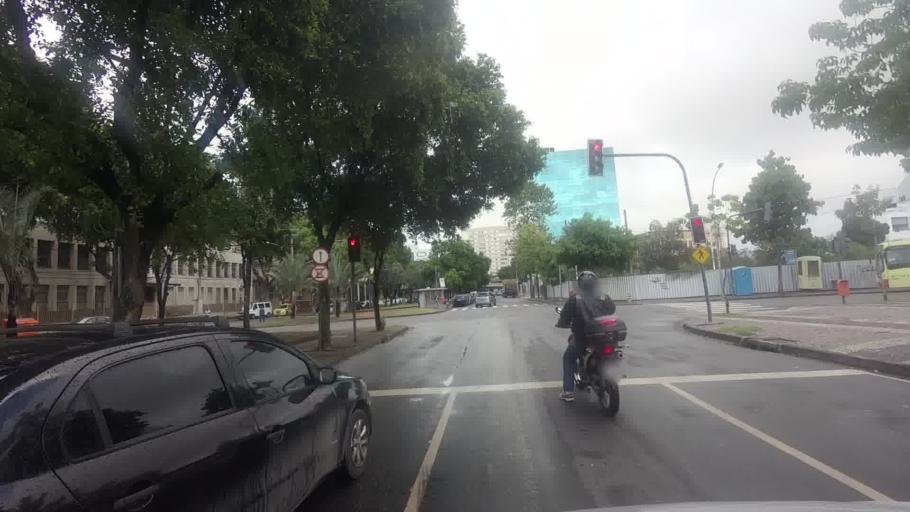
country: BR
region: Rio de Janeiro
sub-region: Rio De Janeiro
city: Rio de Janeiro
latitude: -22.9136
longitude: -43.2081
